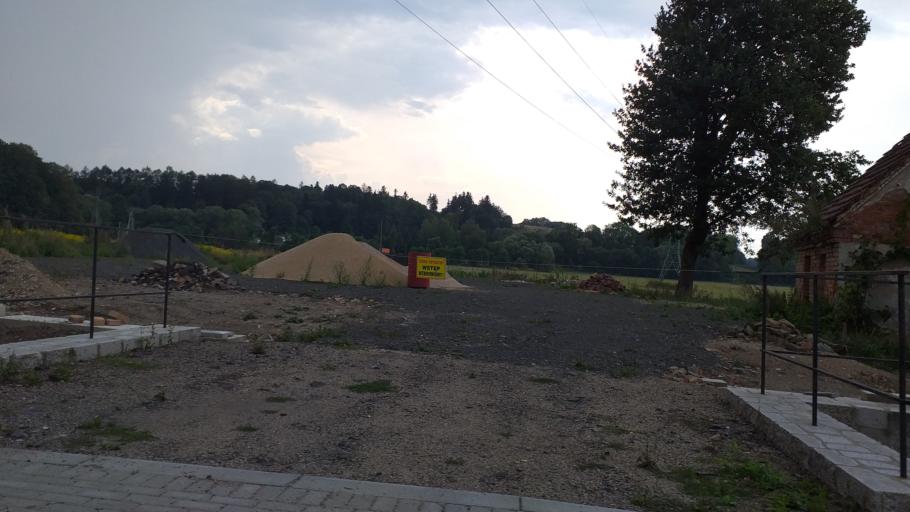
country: PL
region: Lower Silesian Voivodeship
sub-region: Powiat lubanski
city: Lesna
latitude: 51.0394
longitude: 15.2597
